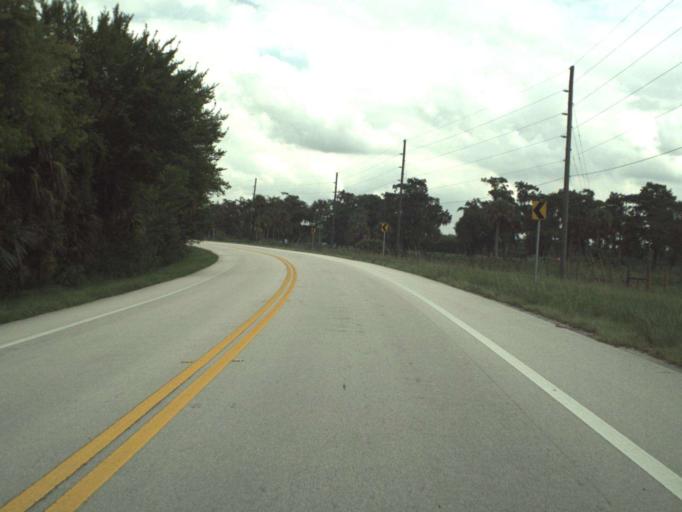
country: US
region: Florida
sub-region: Okeechobee County
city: Taylor Creek
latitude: 27.0985
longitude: -80.6572
